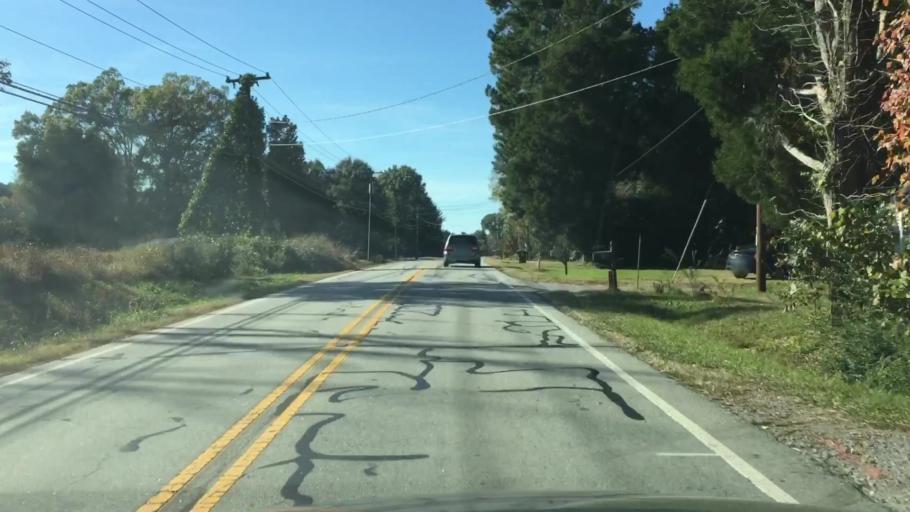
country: US
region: North Carolina
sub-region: Rowan County
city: Salisbury
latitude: 35.6612
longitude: -80.5390
